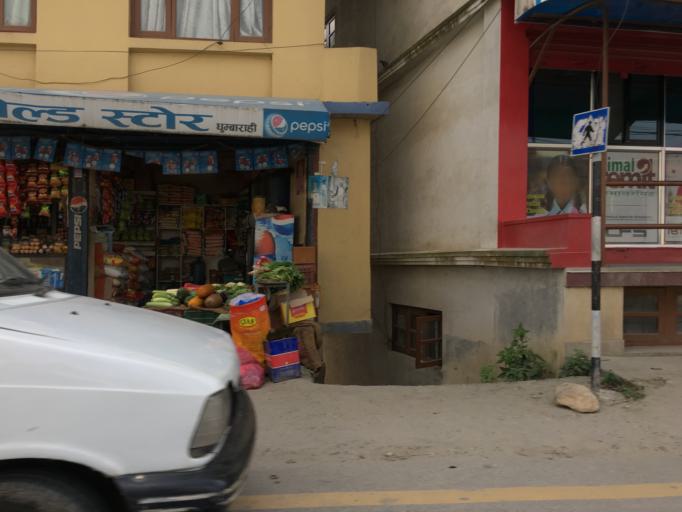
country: NP
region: Central Region
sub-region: Bagmati Zone
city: Kathmandu
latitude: 27.7342
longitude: 85.3459
